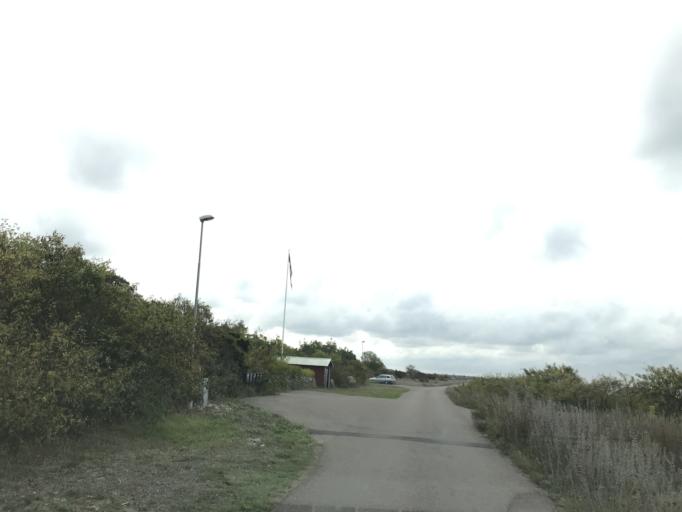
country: SE
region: Kalmar
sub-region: Borgholms Kommun
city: Borgholm
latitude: 57.0582
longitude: 16.8380
